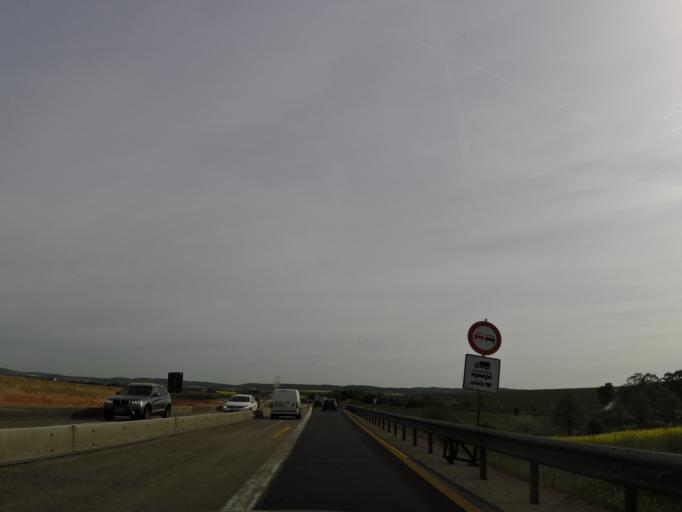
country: DE
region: Lower Saxony
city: Bockenem
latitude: 51.9739
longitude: 10.1490
